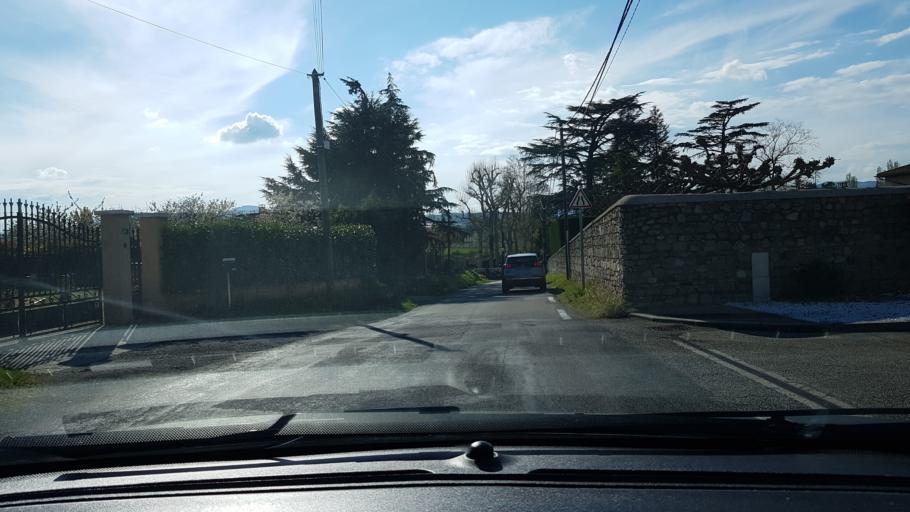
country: FR
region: Rhone-Alpes
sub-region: Departement du Rhone
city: Orlienas
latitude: 45.6643
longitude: 4.7254
